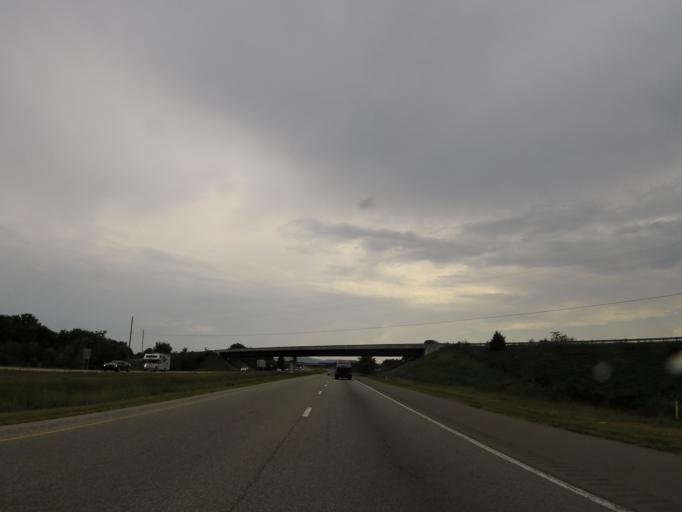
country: US
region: Tennessee
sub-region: Rutherford County
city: Murfreesboro
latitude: 35.8724
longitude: -86.4988
